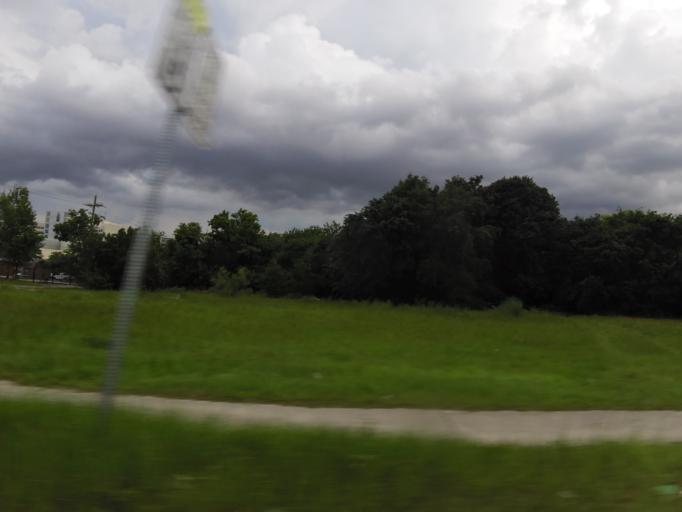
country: US
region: Florida
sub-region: Duval County
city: Jacksonville
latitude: 30.3513
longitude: -81.6612
